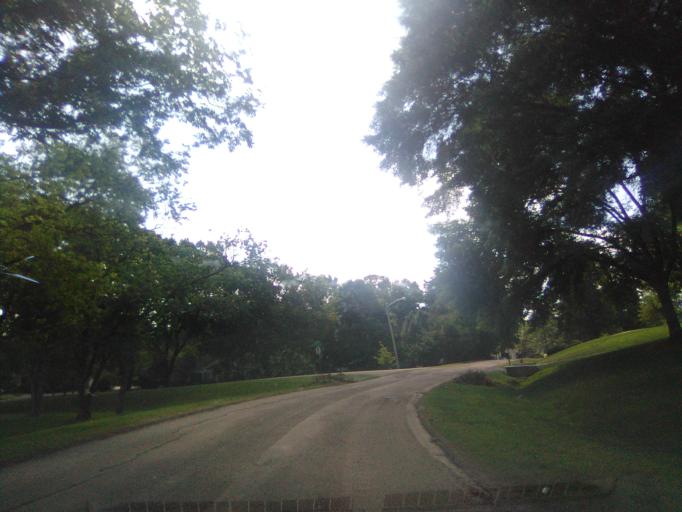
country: US
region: Tennessee
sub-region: Davidson County
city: Belle Meade
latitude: 36.1082
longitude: -86.8703
